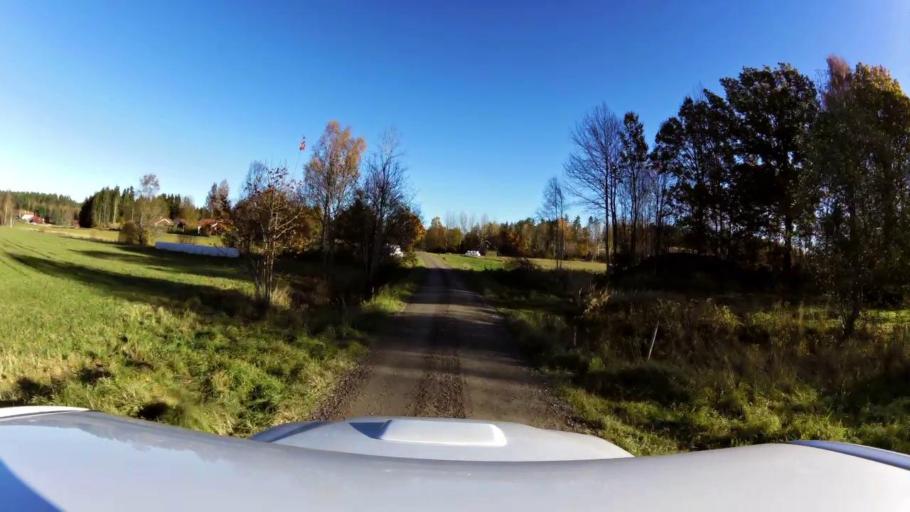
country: SE
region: OEstergoetland
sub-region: Linkopings Kommun
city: Ljungsbro
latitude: 58.5276
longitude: 15.4933
